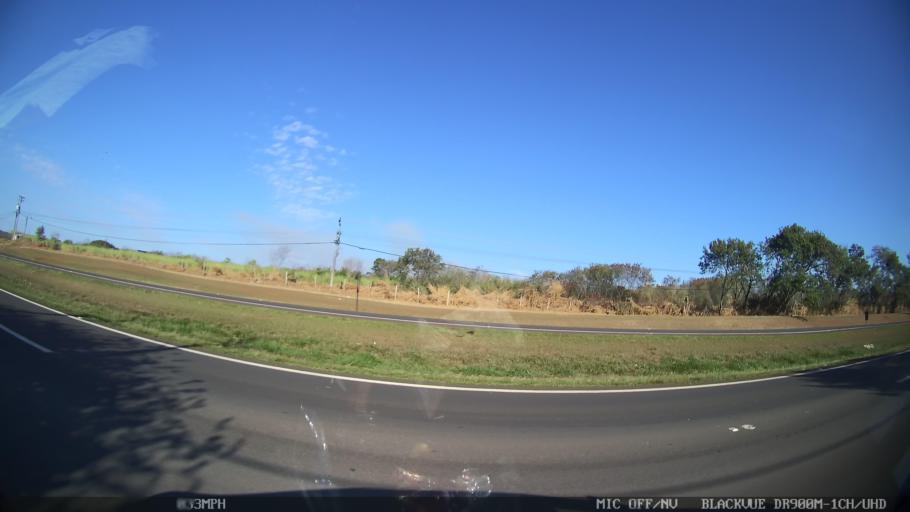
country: BR
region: Sao Paulo
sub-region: Piracicaba
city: Piracicaba
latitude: -22.6646
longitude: -47.6192
